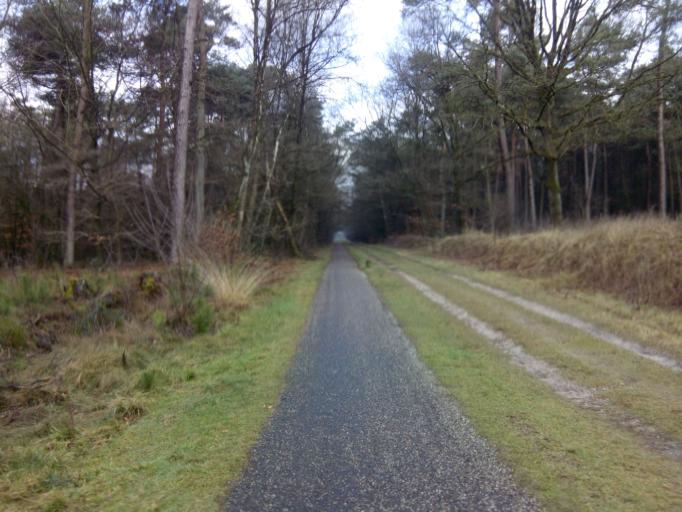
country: NL
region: Utrecht
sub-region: Gemeente Utrechtse Heuvelrug
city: Overberg
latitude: 52.0066
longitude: 5.5020
